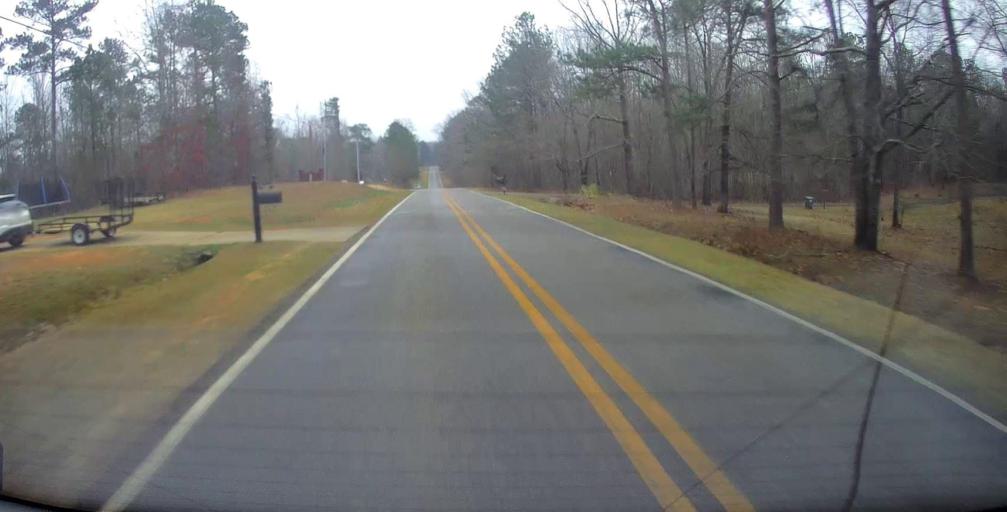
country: US
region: Georgia
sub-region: Lamar County
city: Barnesville
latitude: 33.0672
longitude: -84.1235
